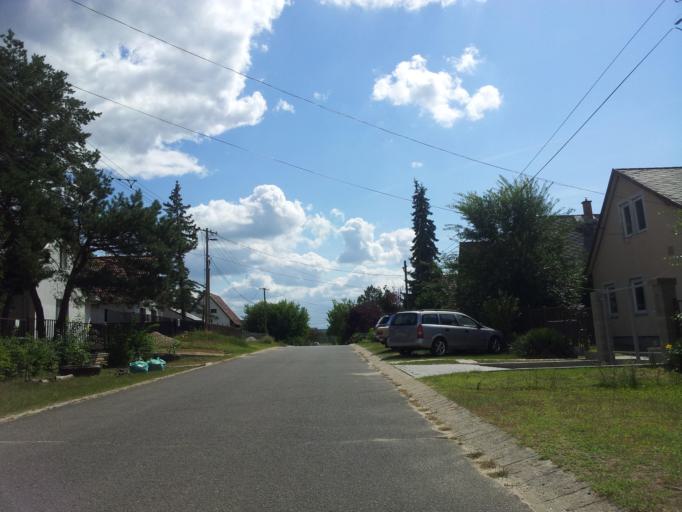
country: HU
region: Pest
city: Veresegyhaz
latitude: 47.6351
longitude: 19.2750
